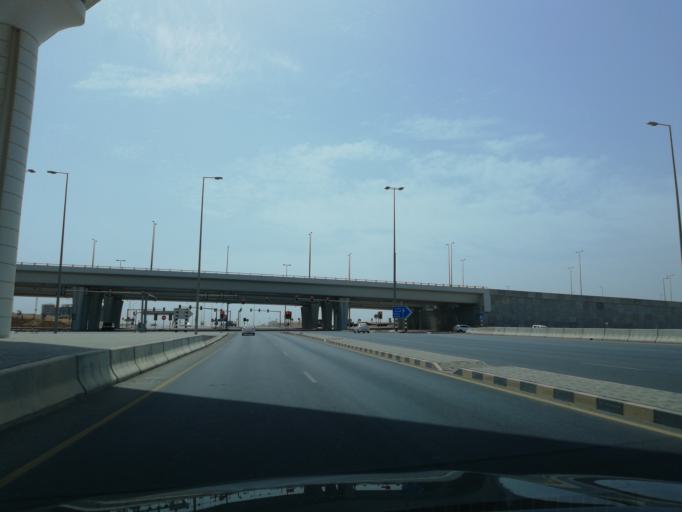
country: OM
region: Muhafazat Masqat
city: Bawshar
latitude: 23.5832
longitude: 58.3342
